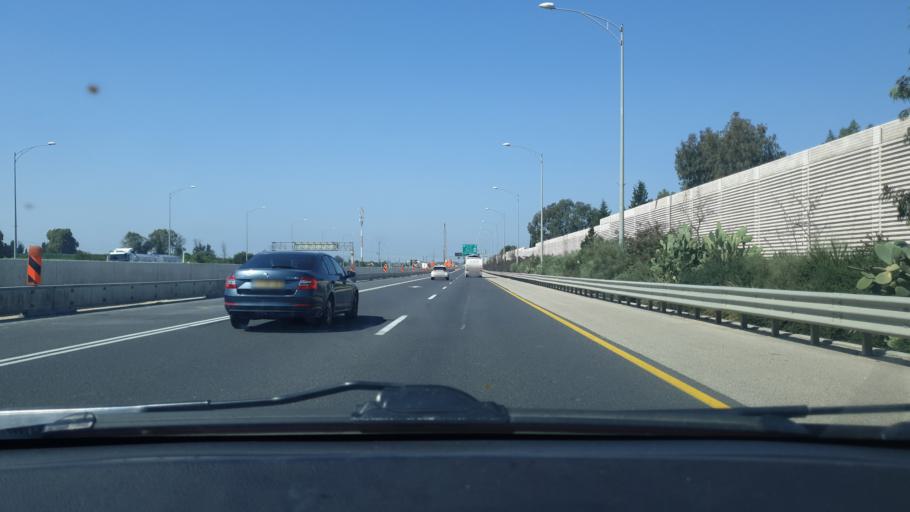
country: IL
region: Central District
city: Ness Ziona
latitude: 31.9288
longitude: 34.8265
